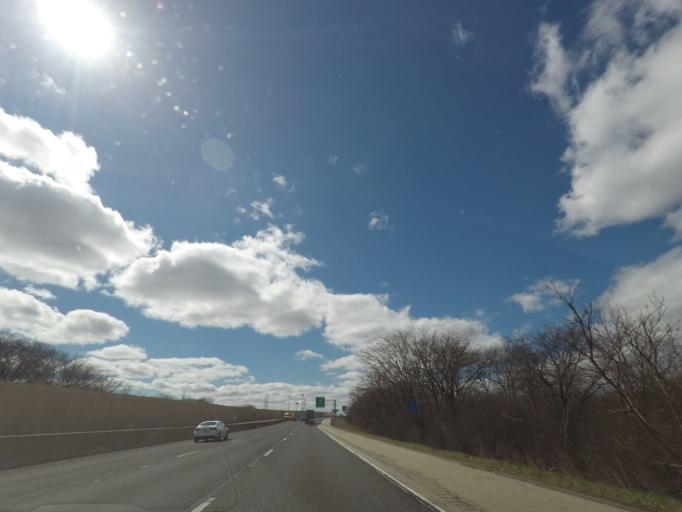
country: US
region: Illinois
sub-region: Will County
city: Crystal Lawns
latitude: 41.5937
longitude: -88.1632
